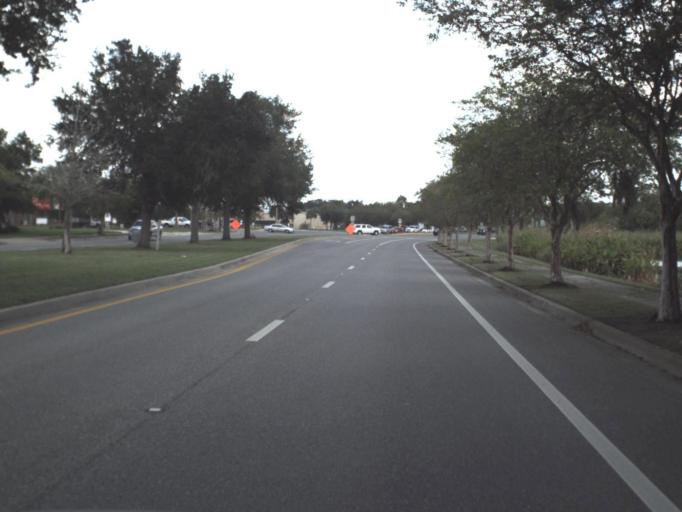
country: US
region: Florida
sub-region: Sarasota County
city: North Sarasota
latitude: 27.3871
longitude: -82.5379
